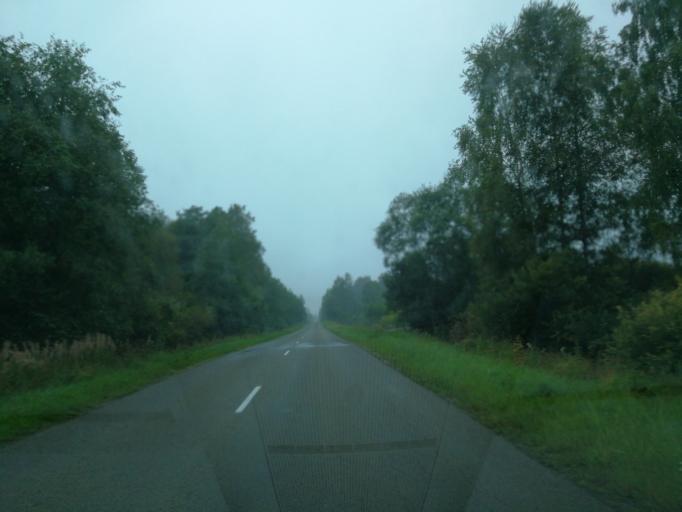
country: LV
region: Preilu Rajons
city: Jaunaglona
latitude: 56.2609
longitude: 26.9913
